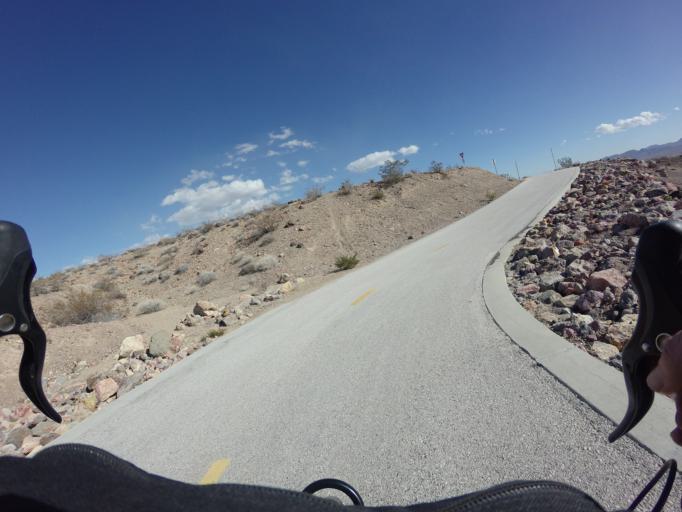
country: US
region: Nevada
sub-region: Clark County
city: Boulder City
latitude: 35.9718
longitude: -114.8750
